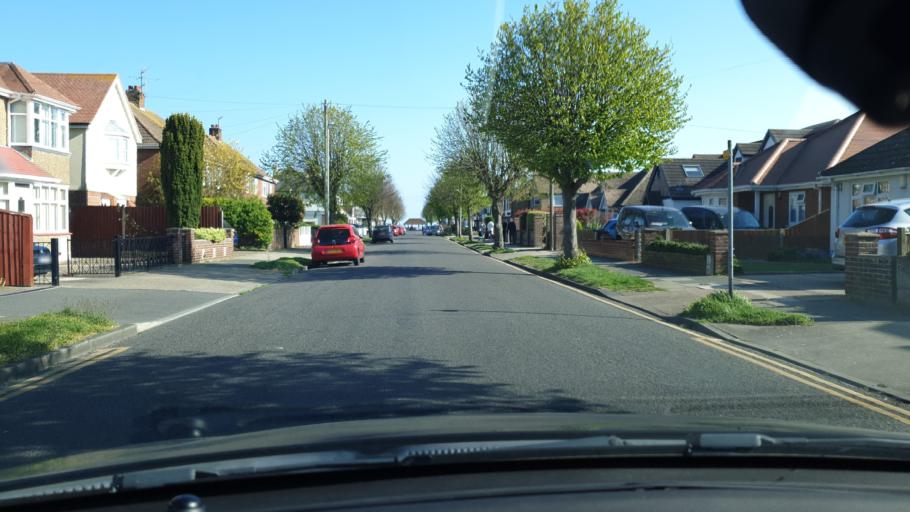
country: GB
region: England
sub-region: Essex
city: Clacton-on-Sea
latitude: 51.8006
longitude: 1.1833
